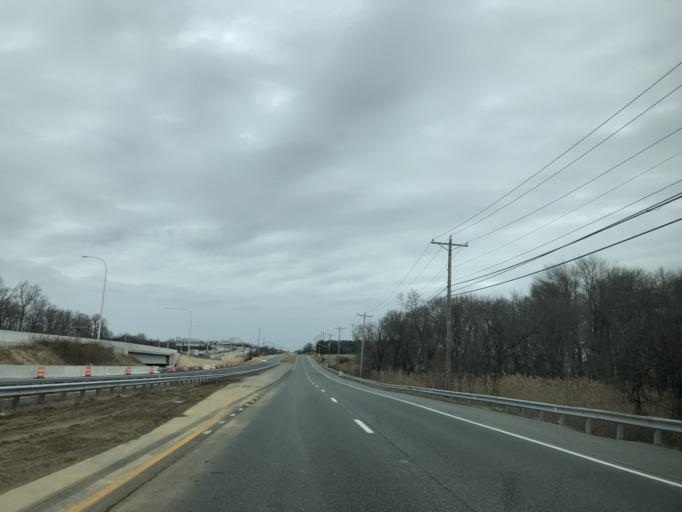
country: US
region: Delaware
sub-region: New Castle County
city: Delaware City
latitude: 39.5344
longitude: -75.6488
